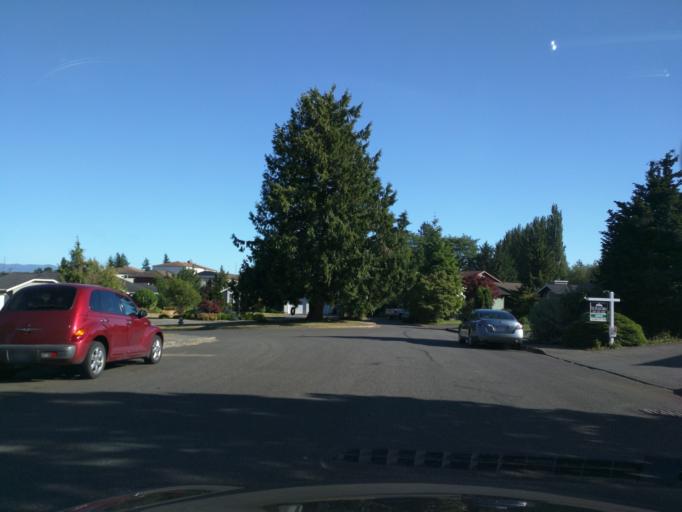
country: US
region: Washington
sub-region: Whatcom County
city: Lynden
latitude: 48.9500
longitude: -122.4571
